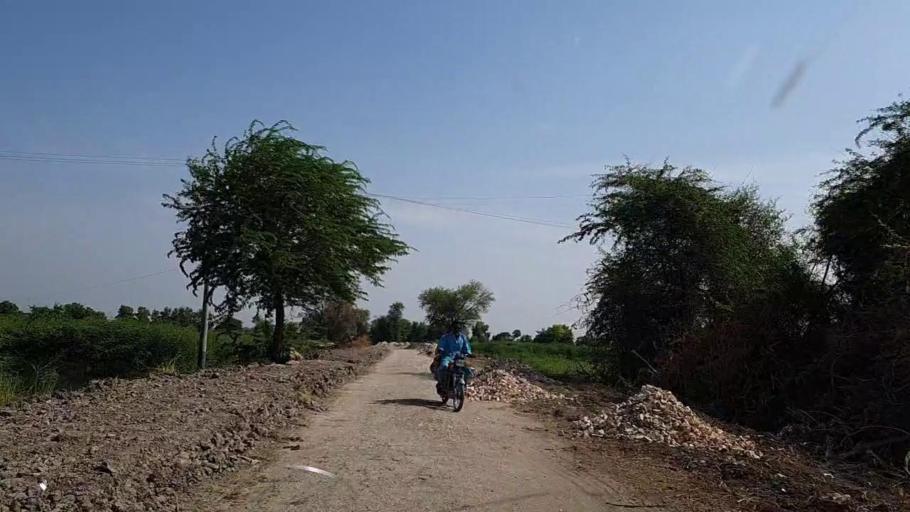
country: PK
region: Sindh
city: Khanpur
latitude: 27.7450
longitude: 69.3414
